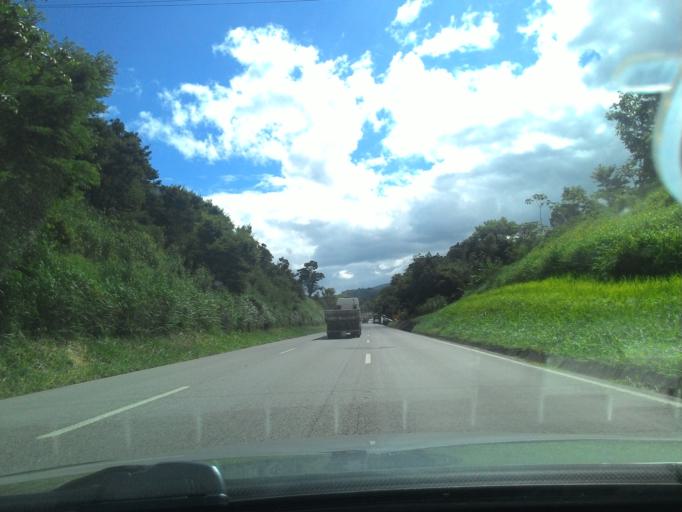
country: BR
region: Sao Paulo
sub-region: Cajati
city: Cajati
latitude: -24.7816
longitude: -48.1760
